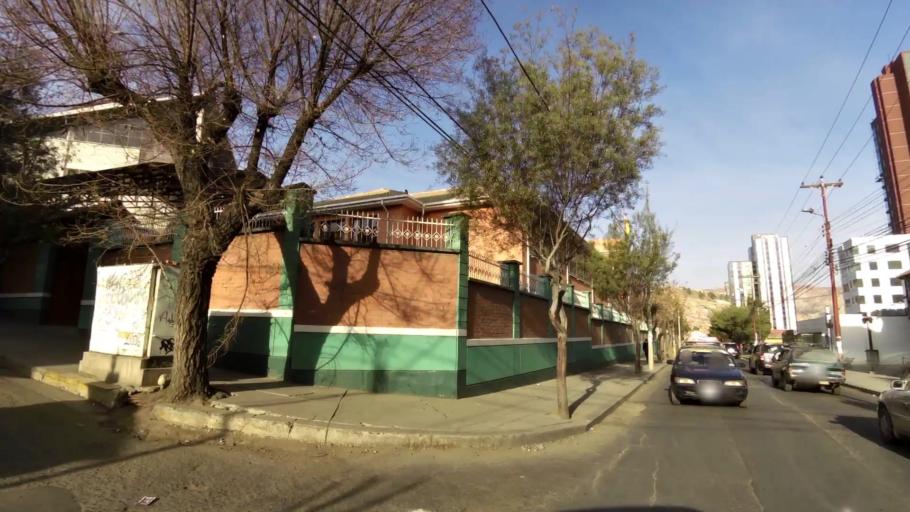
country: BO
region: La Paz
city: La Paz
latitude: -16.5279
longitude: -68.1036
